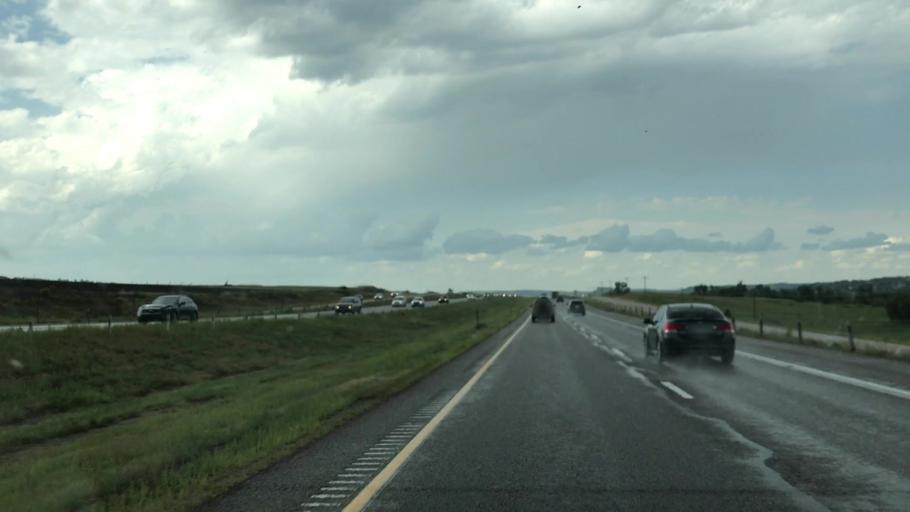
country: US
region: Colorado
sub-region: Douglas County
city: Castle Rock
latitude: 39.3201
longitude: -104.8826
